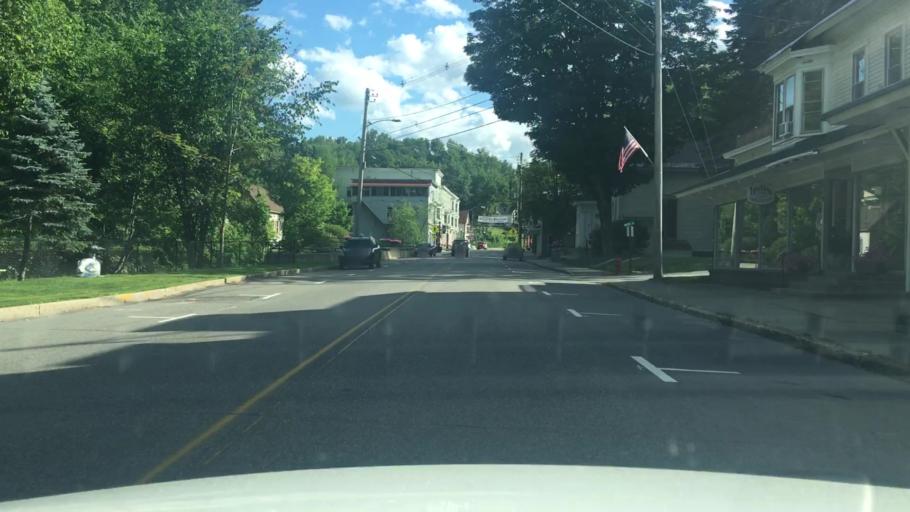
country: US
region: Maine
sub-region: Franklin County
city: Wilton
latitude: 44.5888
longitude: -70.2303
